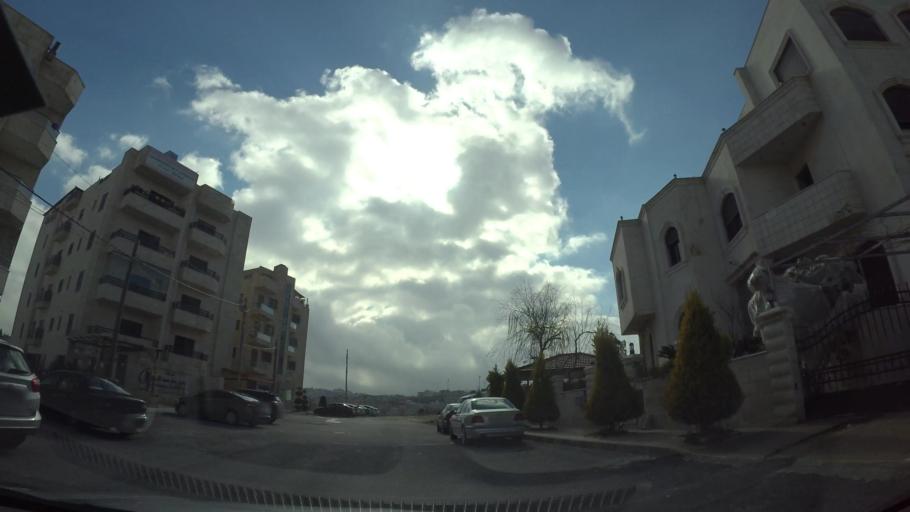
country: JO
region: Amman
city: Al Jubayhah
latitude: 32.0396
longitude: 35.8750
